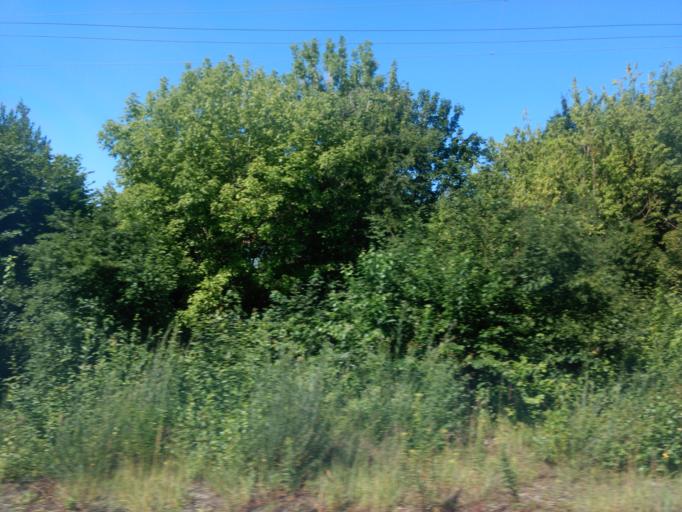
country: DE
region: Bavaria
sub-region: Upper Bavaria
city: Unterfoehring
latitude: 48.1640
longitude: 11.6471
